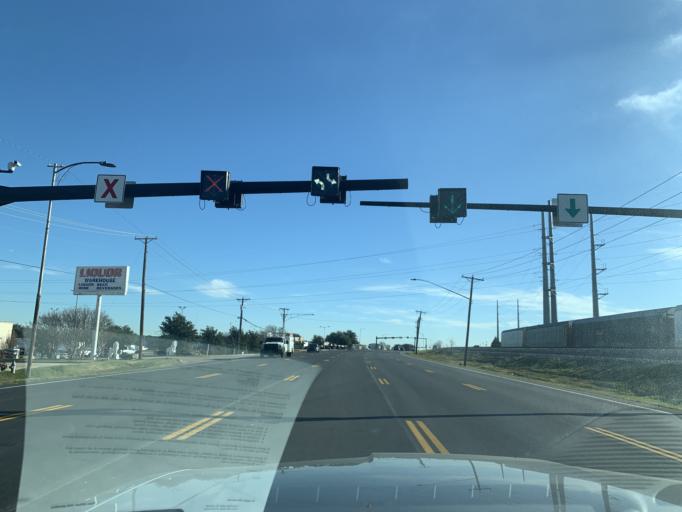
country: US
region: Texas
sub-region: Tarrant County
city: Arlington
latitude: 32.7429
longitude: -97.0752
